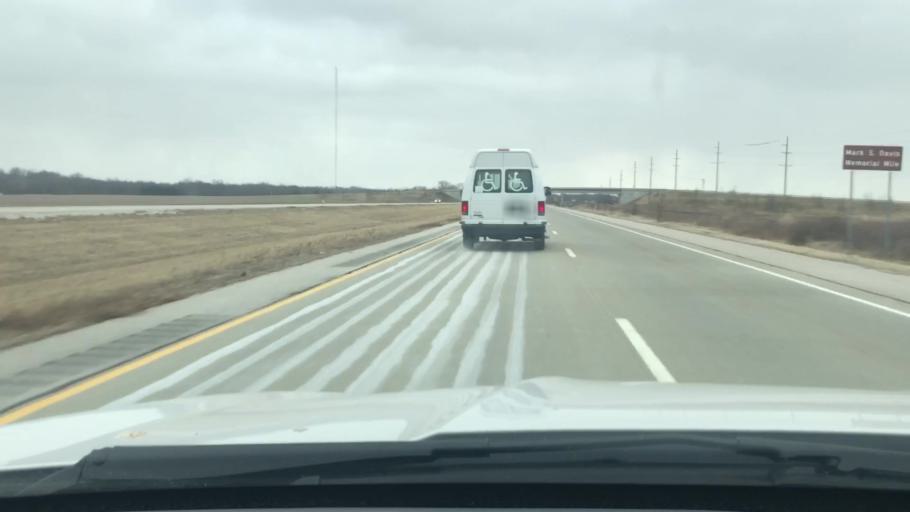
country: US
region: Indiana
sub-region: Tippecanoe County
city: Battle Ground
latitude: 40.4975
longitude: -86.7384
